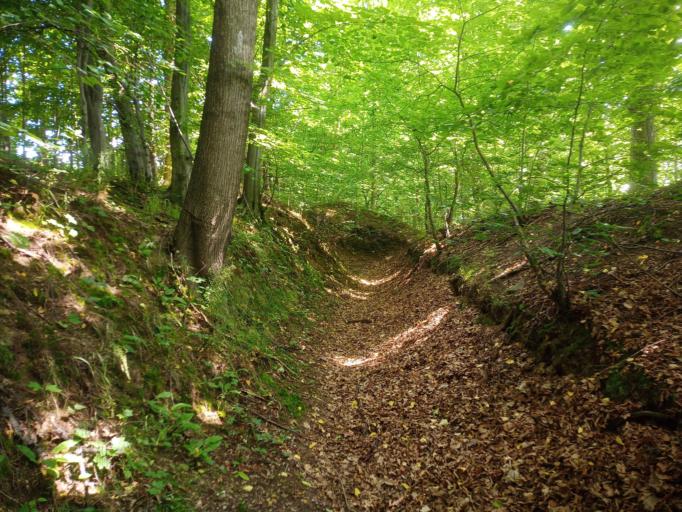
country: PL
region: Lower Silesian Voivodeship
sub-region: Powiat lubanski
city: Lesna
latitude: 51.0279
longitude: 15.2744
